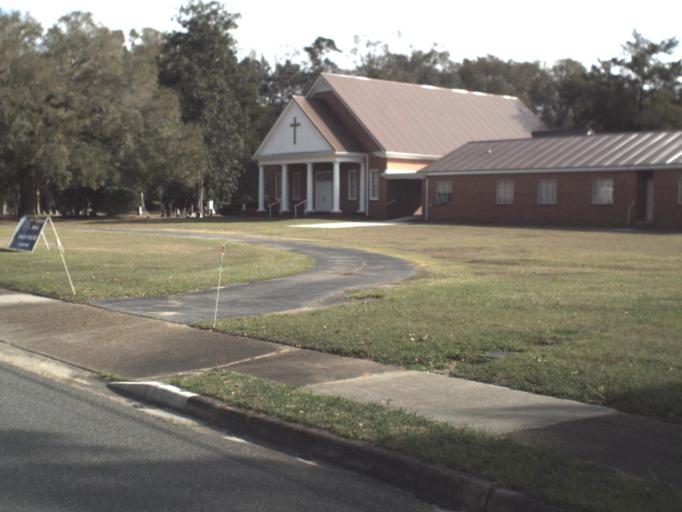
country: US
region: Florida
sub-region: Jackson County
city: Malone
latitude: 30.8666
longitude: -85.1626
